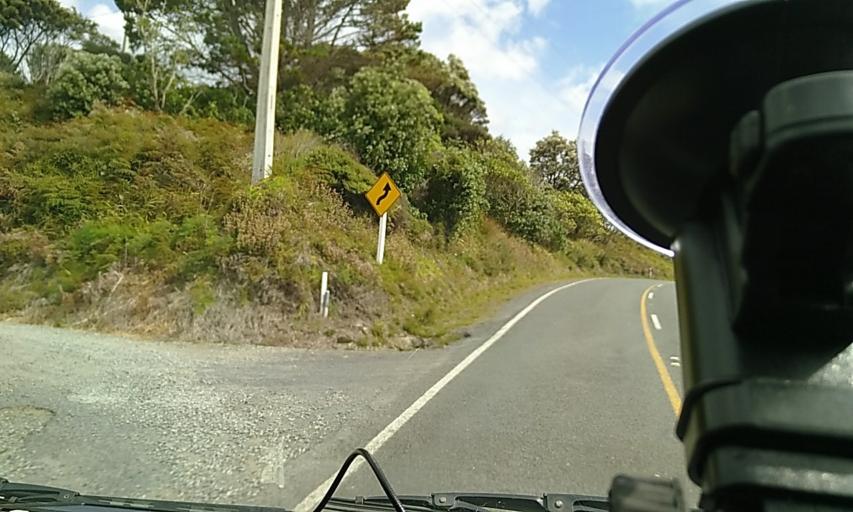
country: NZ
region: Northland
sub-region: Far North District
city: Ahipara
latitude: -35.5174
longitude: 173.3884
